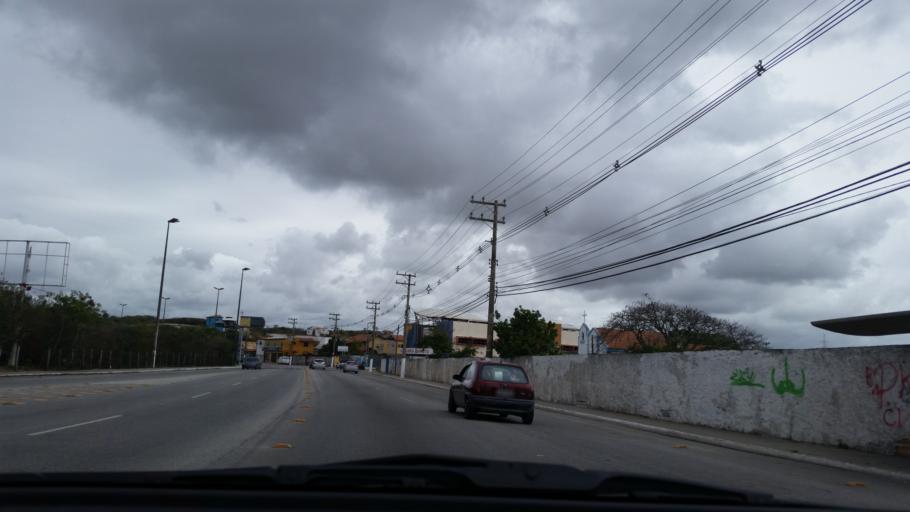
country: BR
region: Rio de Janeiro
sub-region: Cabo Frio
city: Cabo Frio
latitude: -22.8629
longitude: -42.0329
